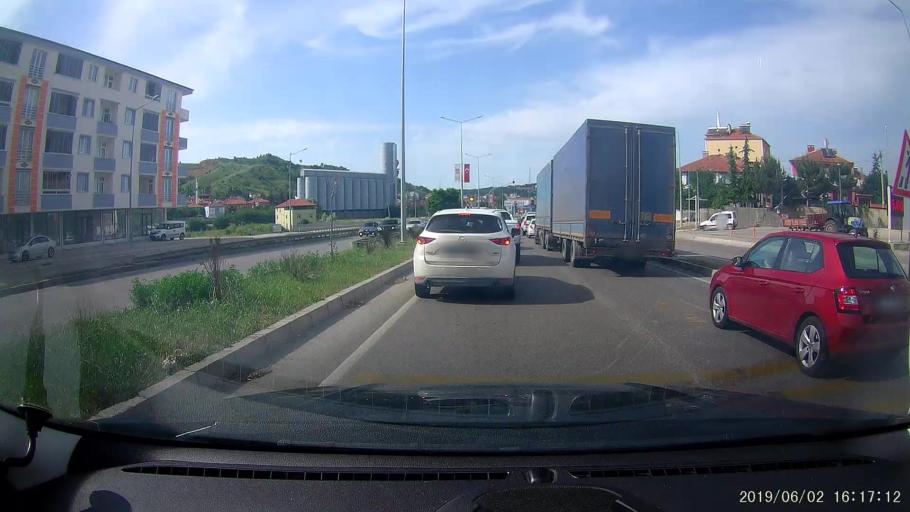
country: TR
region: Samsun
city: Havza
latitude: 40.9590
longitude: 35.6660
